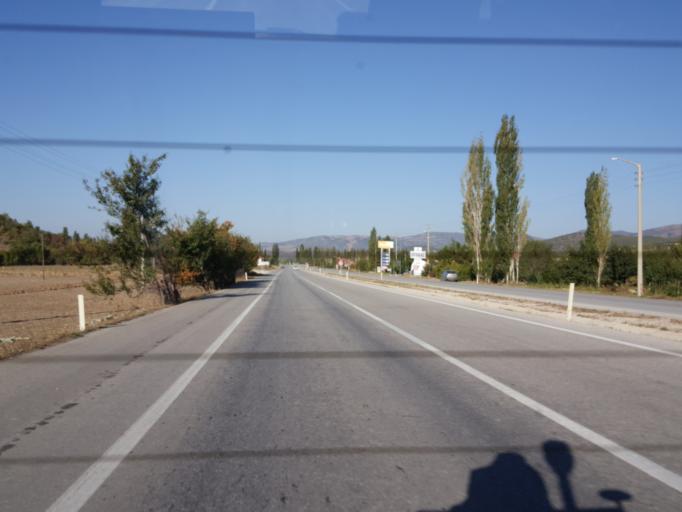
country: TR
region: Amasya
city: Ezinepazari
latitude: 40.5712
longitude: 36.1293
